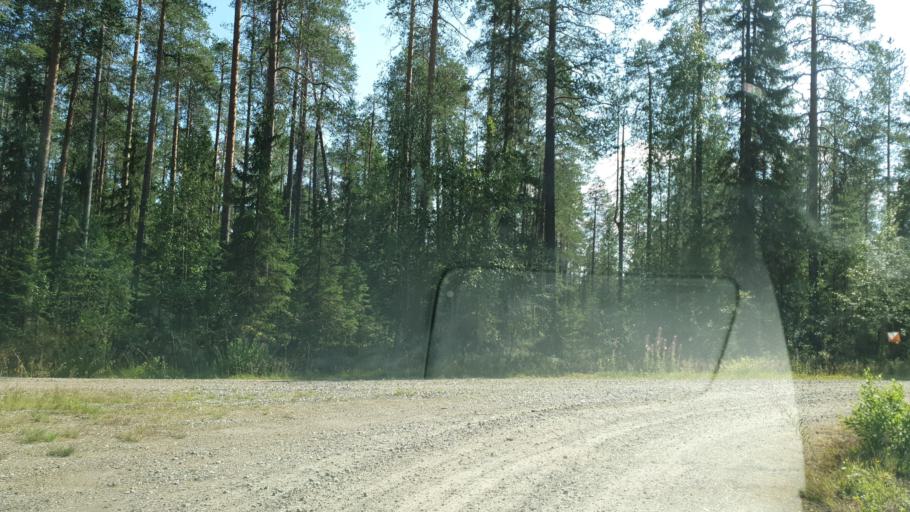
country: FI
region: Kainuu
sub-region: Kehys-Kainuu
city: Kuhmo
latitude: 63.9649
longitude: 29.5440
